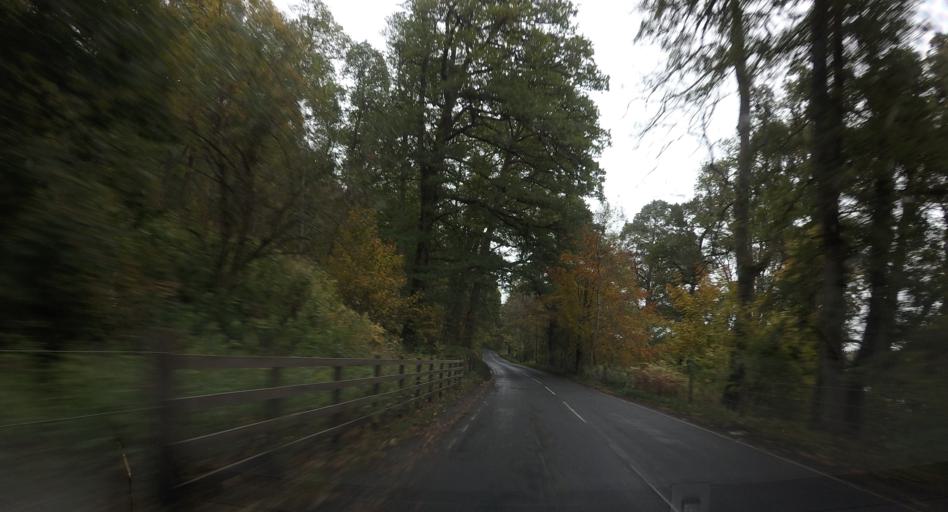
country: GB
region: Scotland
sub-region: Perth and Kinross
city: Bankfoot
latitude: 56.5465
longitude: -3.5072
